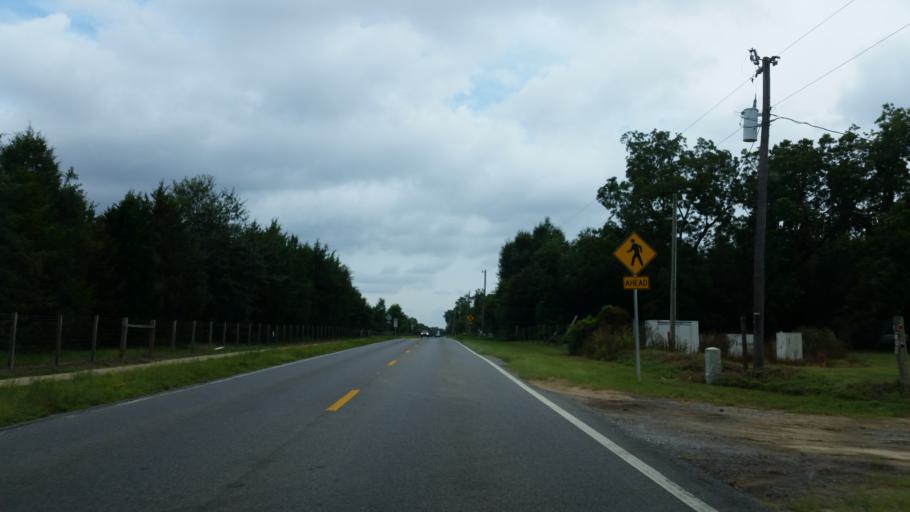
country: US
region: Florida
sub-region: Santa Rosa County
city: Pace
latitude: 30.6267
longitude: -87.1482
